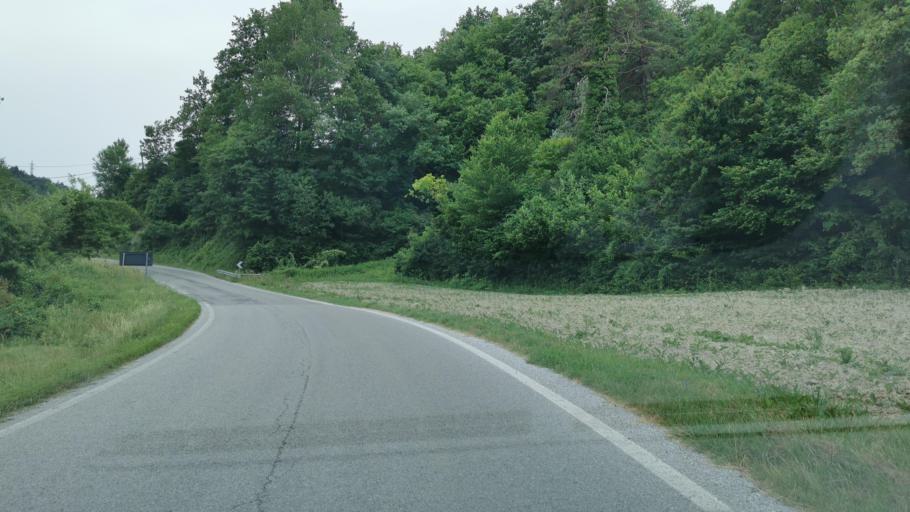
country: IT
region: Piedmont
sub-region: Provincia di Cuneo
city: Torresina
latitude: 44.4144
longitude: 8.0474
